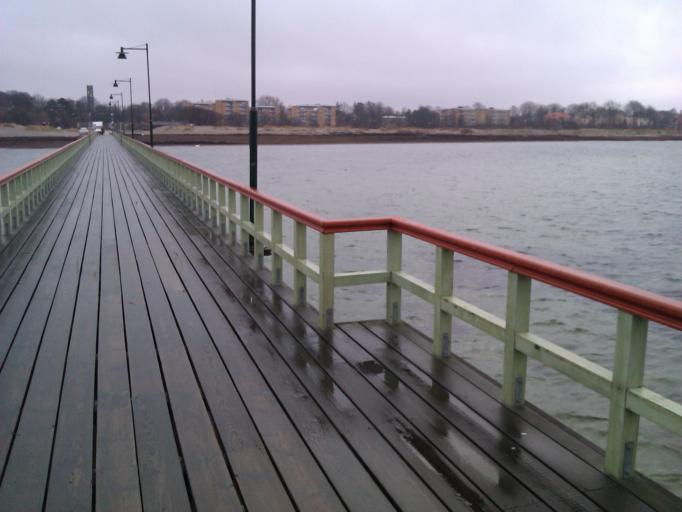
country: SE
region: Skane
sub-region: Malmo
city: Malmoe
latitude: 55.6048
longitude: 12.9658
